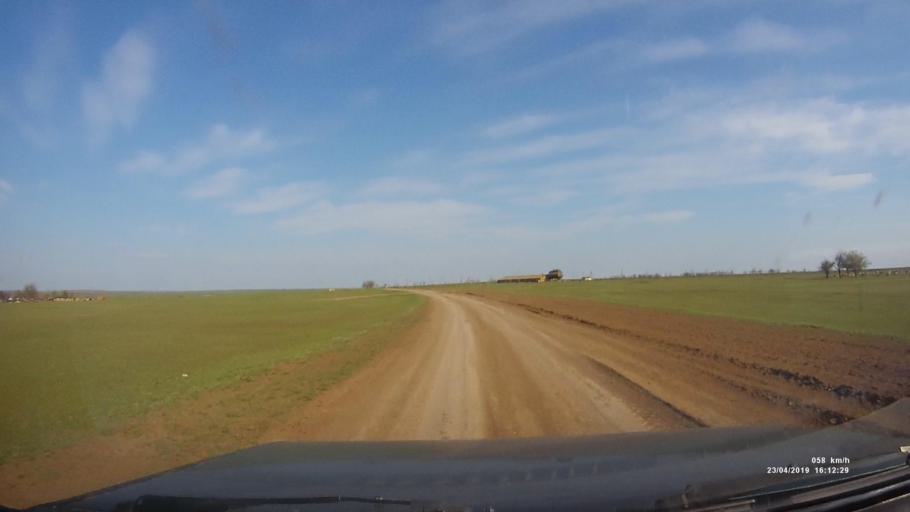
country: RU
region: Kalmykiya
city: Priyutnoye
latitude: 46.4662
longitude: 43.1267
